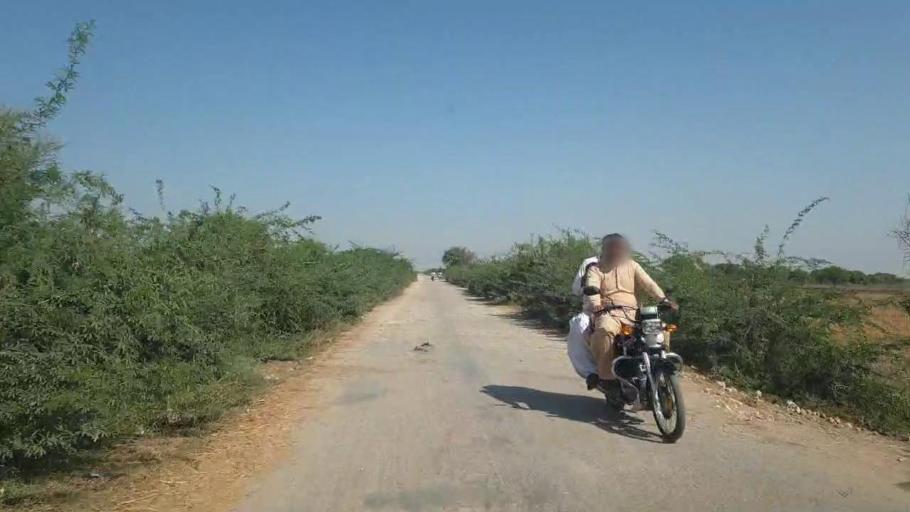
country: PK
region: Sindh
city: Tando Bago
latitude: 24.8214
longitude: 68.9856
